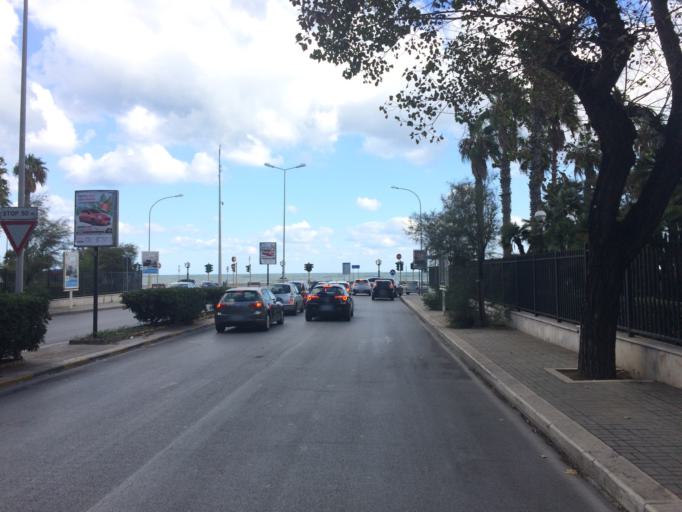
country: IT
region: Apulia
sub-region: Provincia di Bari
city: Bari
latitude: 41.1186
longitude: 16.8895
